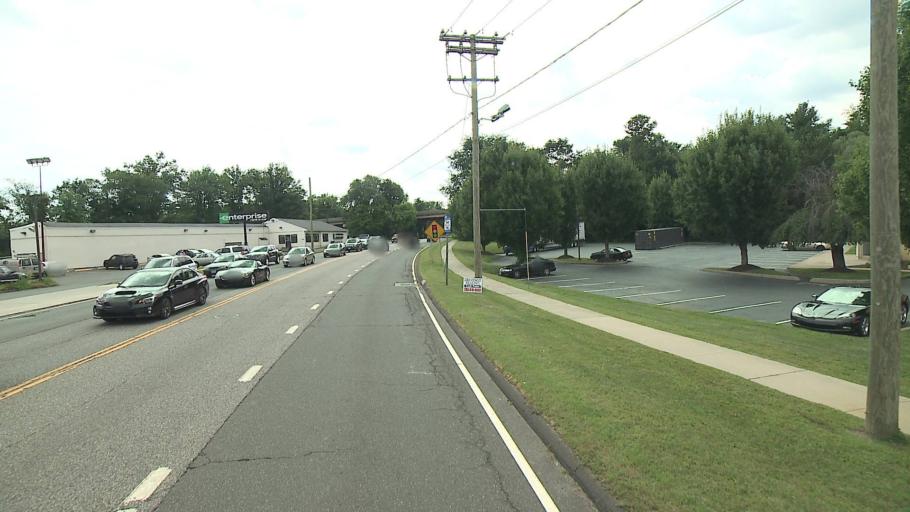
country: US
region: Connecticut
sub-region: Fairfield County
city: Danbury
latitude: 41.4189
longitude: -73.4199
